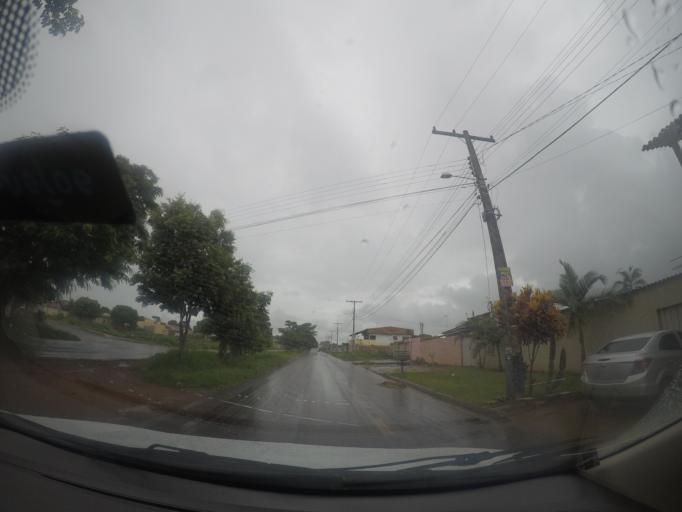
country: BR
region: Goias
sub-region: Trindade
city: Trindade
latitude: -16.6382
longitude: -49.4324
